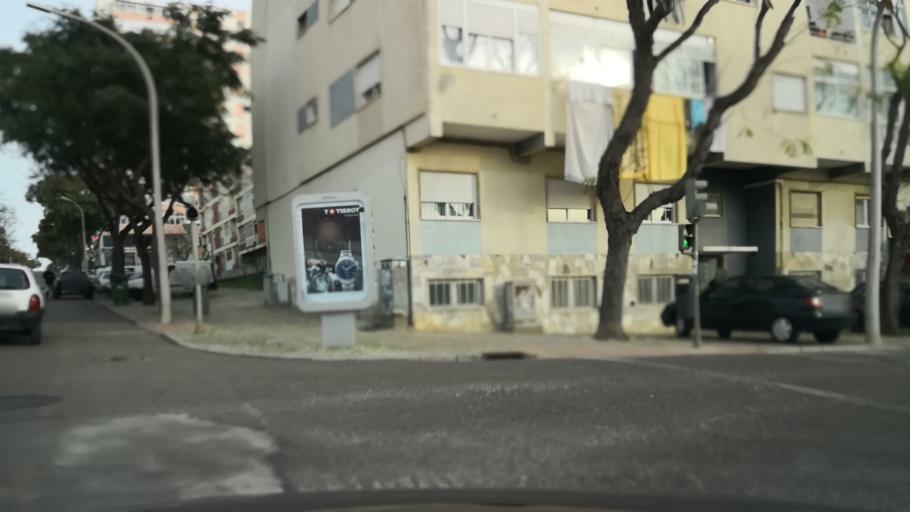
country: PT
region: Setubal
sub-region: Setubal
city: Setubal
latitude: 38.5247
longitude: -8.8824
